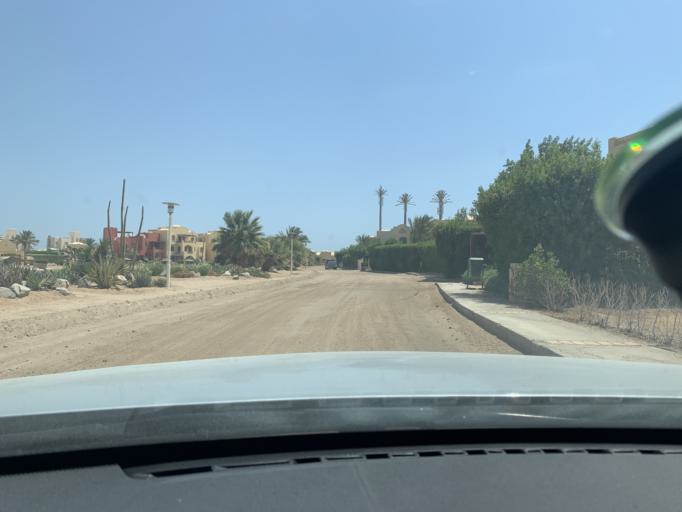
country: EG
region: Red Sea
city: El Gouna
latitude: 27.4051
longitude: 33.6702
